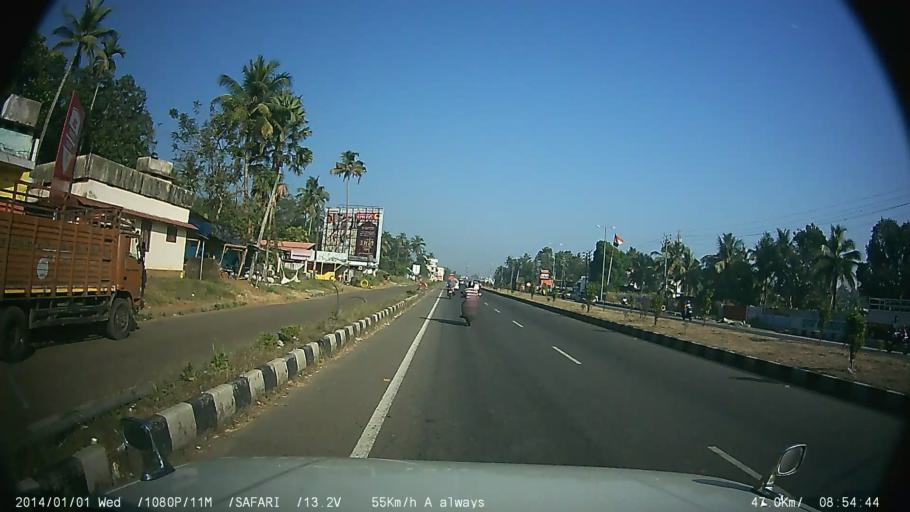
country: IN
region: Kerala
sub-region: Ernakulam
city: Angamali
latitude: 10.2197
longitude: 76.3769
